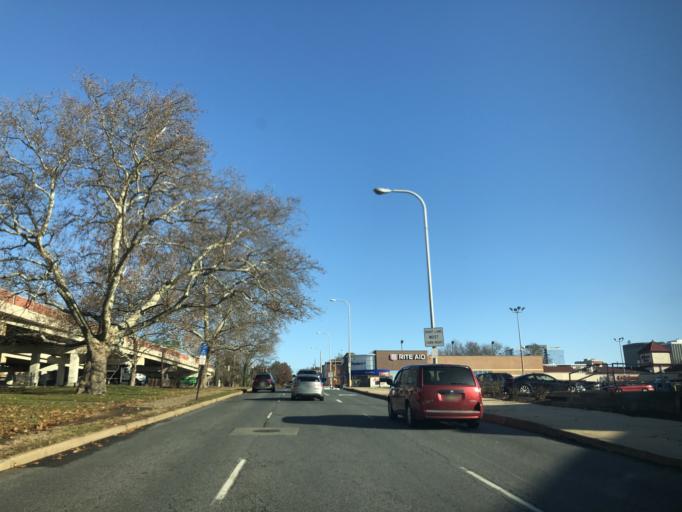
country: US
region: Delaware
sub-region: New Castle County
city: Wilmington
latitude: 39.7425
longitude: -75.5606
